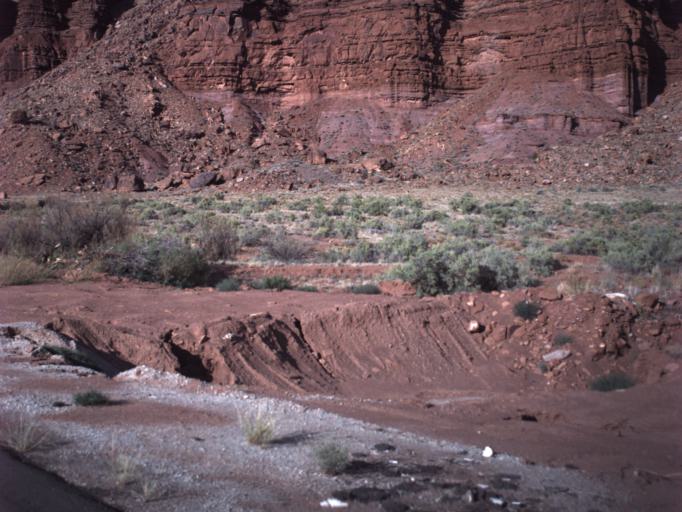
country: US
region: Utah
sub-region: Grand County
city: Moab
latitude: 38.7657
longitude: -109.3202
